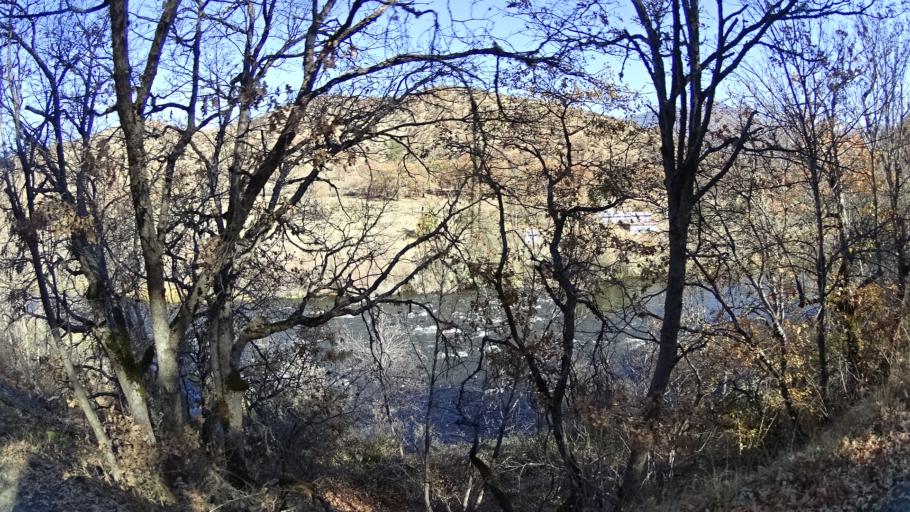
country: US
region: California
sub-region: Siskiyou County
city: Yreka
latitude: 41.8619
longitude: -122.7233
